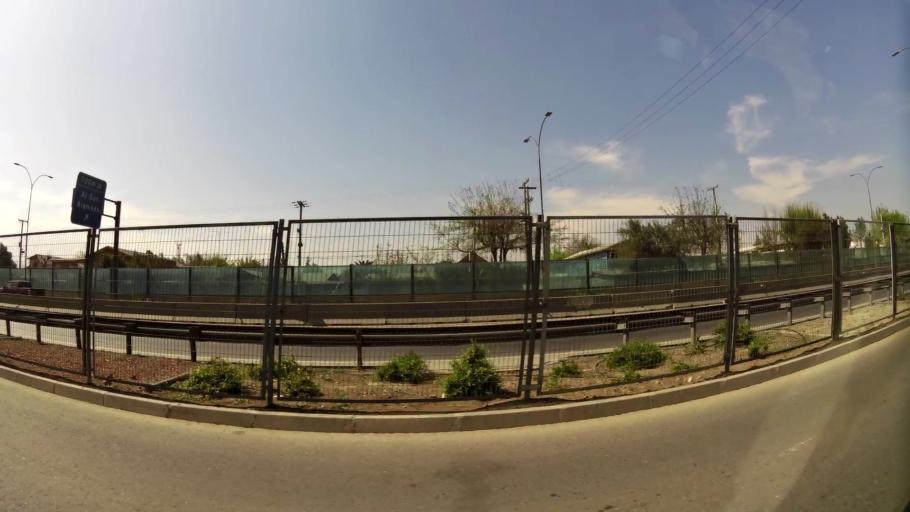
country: CL
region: Santiago Metropolitan
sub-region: Provincia de Santiago
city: Lo Prado
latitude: -33.3872
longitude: -70.6982
